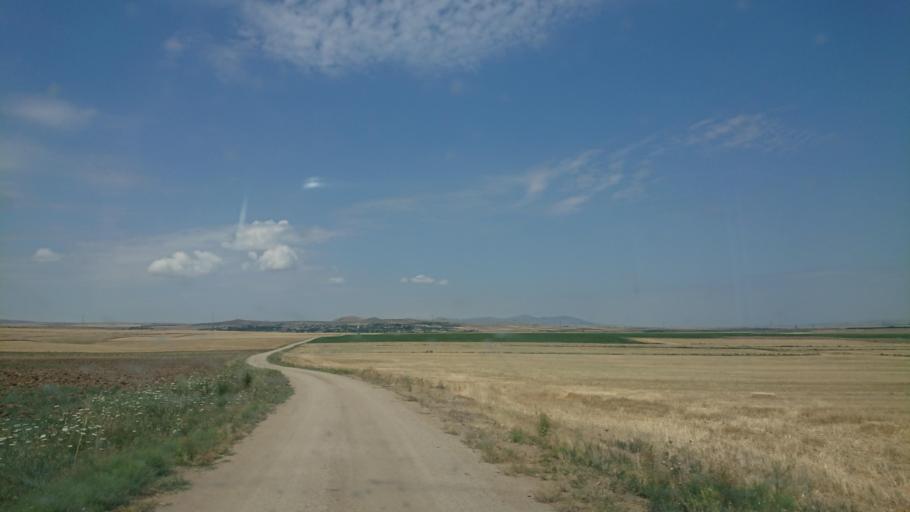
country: TR
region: Aksaray
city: Agacoren
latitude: 38.9560
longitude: 33.9213
